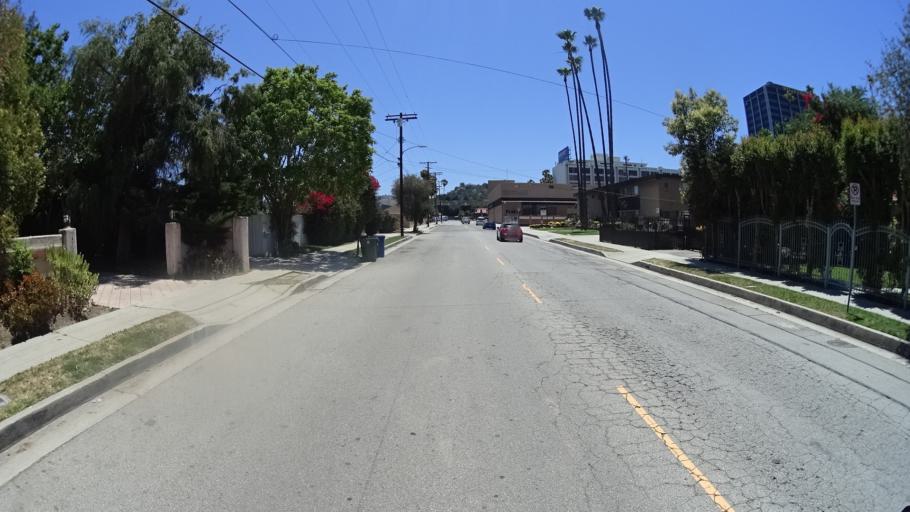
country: US
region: California
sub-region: Los Angeles County
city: Sherman Oaks
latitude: 34.1566
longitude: -118.4750
